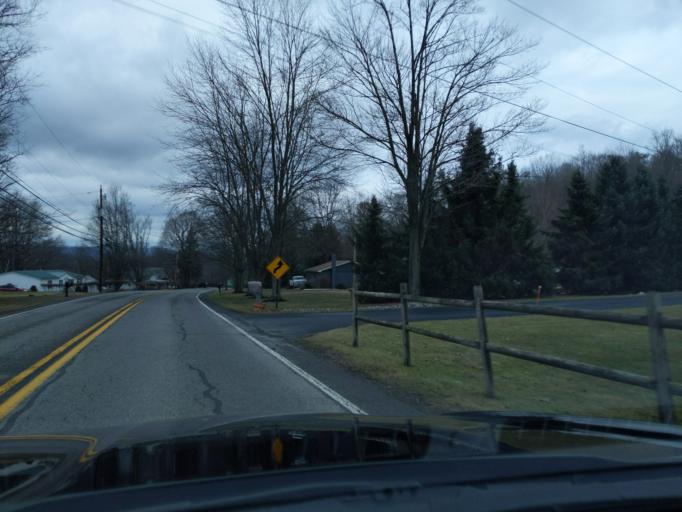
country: US
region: Pennsylvania
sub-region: Blair County
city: Bellwood
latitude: 40.5784
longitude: -78.3451
